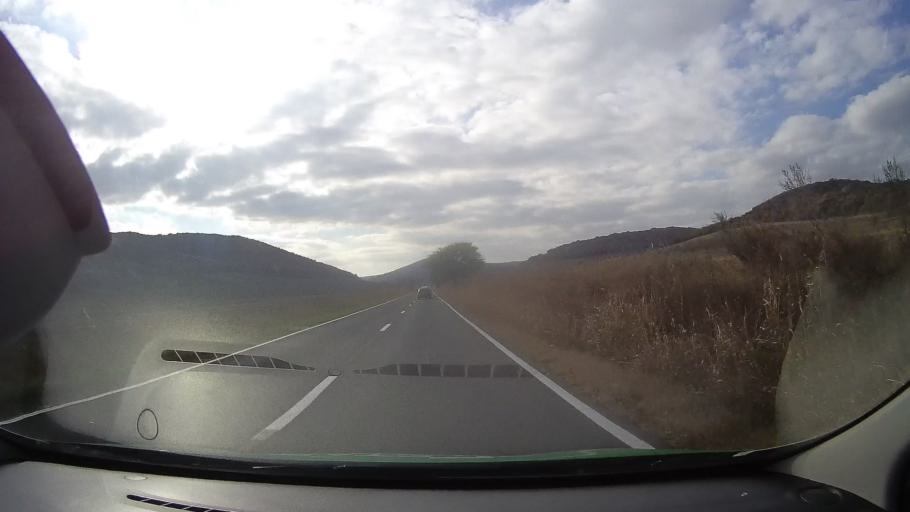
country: RO
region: Tulcea
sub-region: Comuna Ciucurova
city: Ciucurova
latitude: 44.9675
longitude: 28.5338
